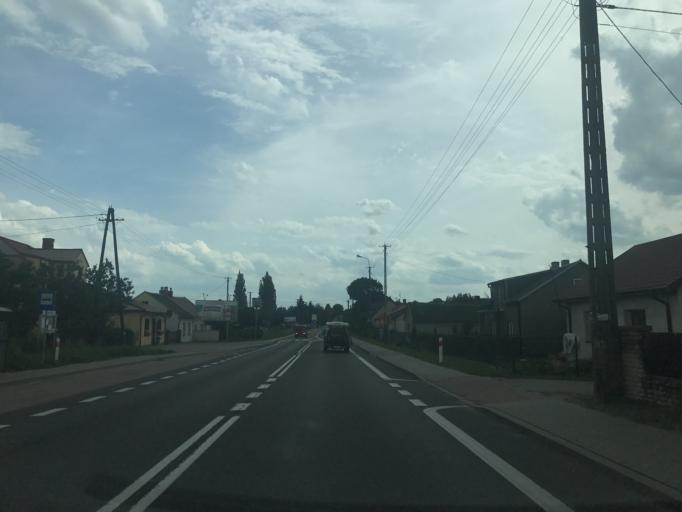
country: PL
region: Masovian Voivodeship
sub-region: Powiat mlawski
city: Wisniewo
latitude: 53.0003
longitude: 20.3295
